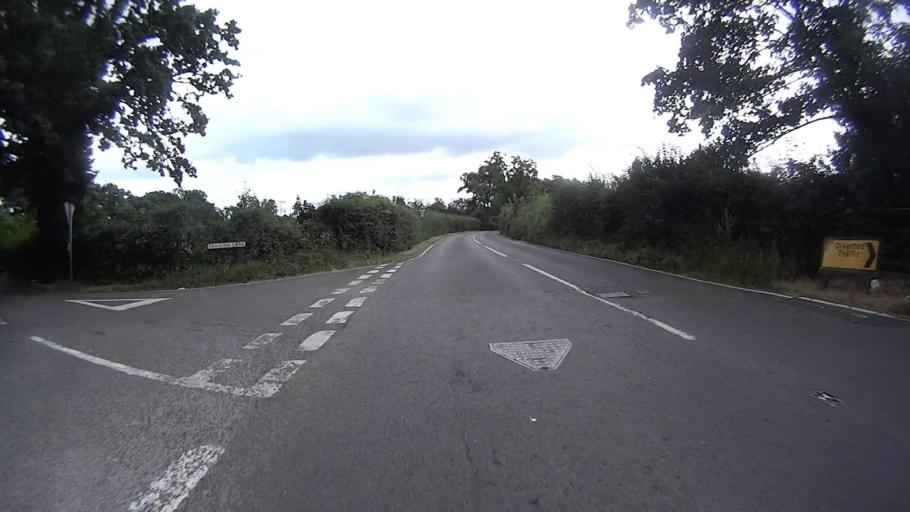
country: GB
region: England
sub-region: Surrey
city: Reigate
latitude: 51.1924
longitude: -0.2403
